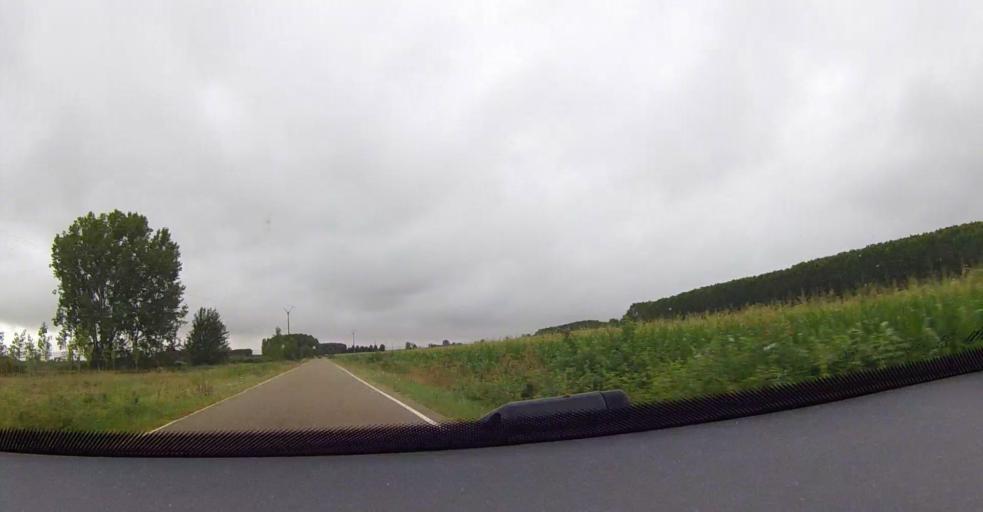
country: ES
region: Castille and Leon
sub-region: Provincia de Palencia
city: Pedrosa de la Vega
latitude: 42.4812
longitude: -4.7282
